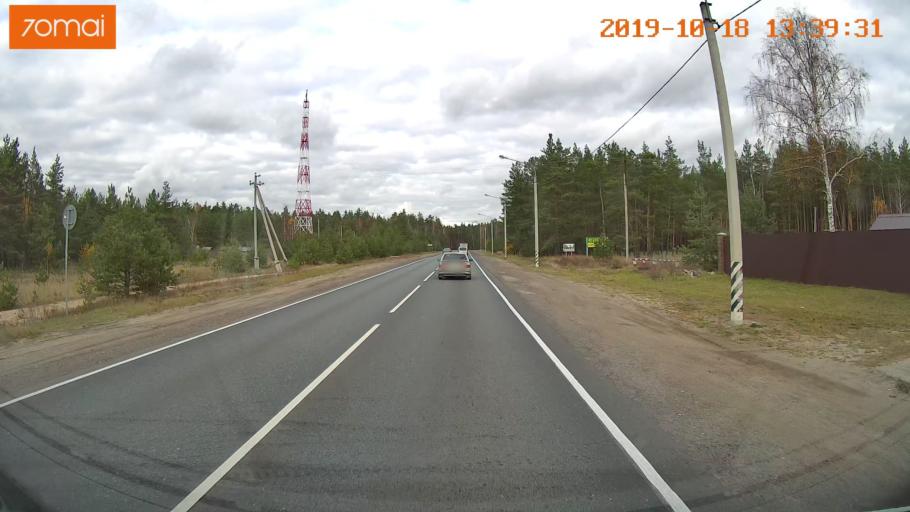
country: RU
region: Rjazan
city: Solotcha
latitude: 54.8998
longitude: 40.0023
